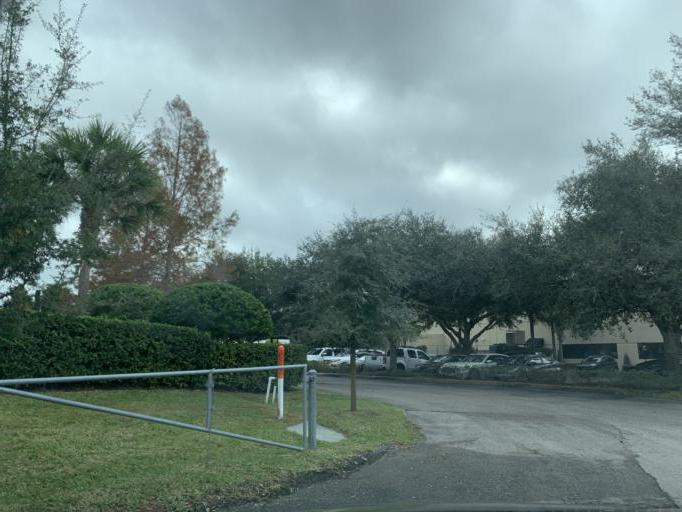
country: US
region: Florida
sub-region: Orange County
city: Eatonville
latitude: 28.6140
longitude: -81.3901
